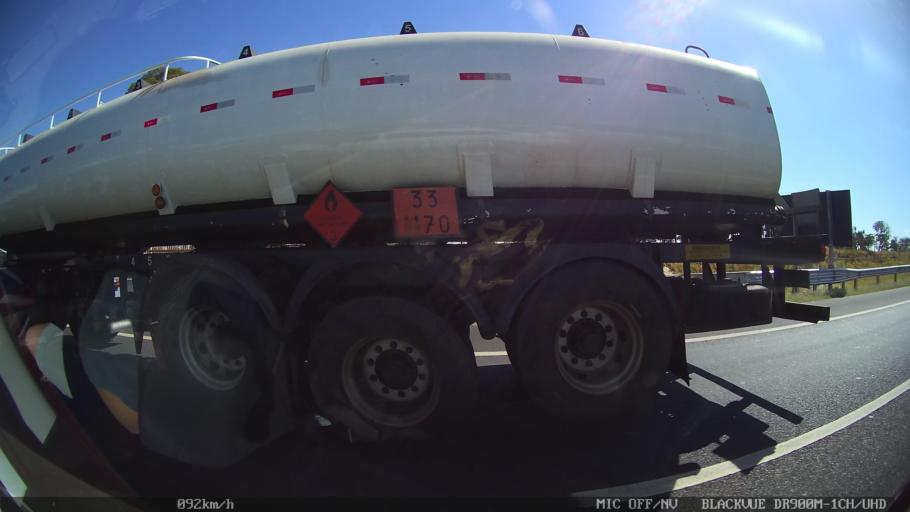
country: BR
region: Sao Paulo
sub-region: Franca
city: Franca
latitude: -20.5261
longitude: -47.4213
